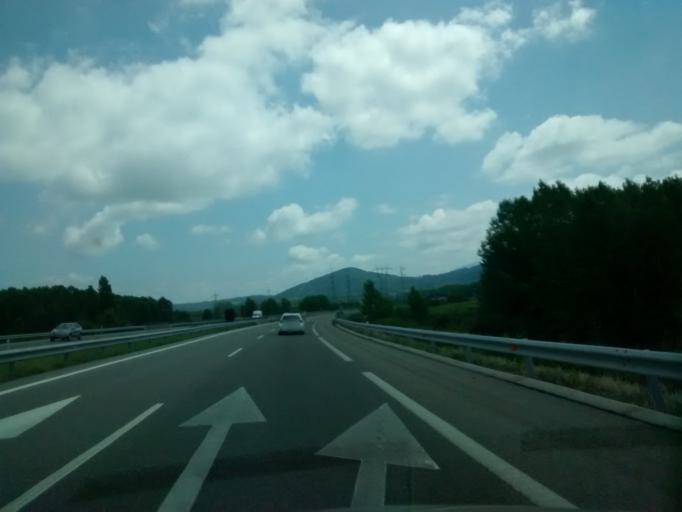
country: ES
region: Castille and Leon
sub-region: Provincia de Leon
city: Camponaraya
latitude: 42.5852
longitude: -6.6360
